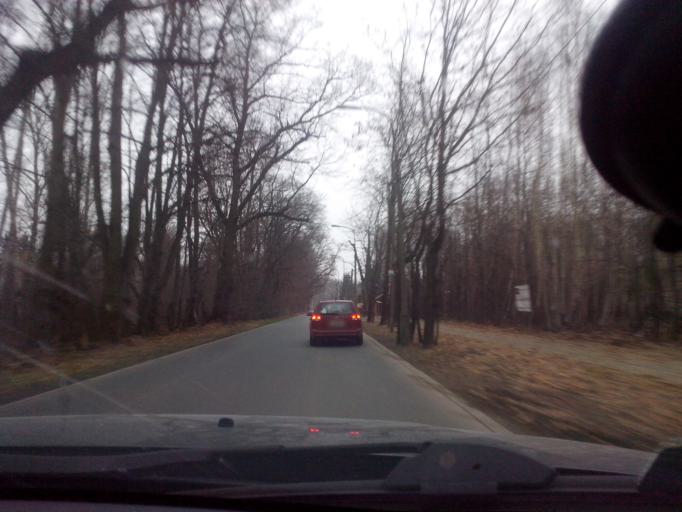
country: PL
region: Masovian Voivodeship
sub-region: Warszawa
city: Bialoleka
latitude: 52.3492
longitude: 20.9724
